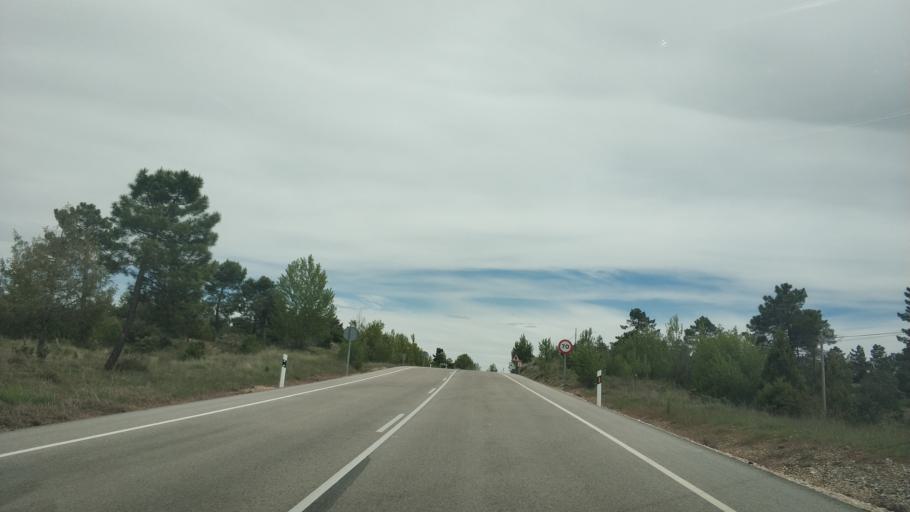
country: ES
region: Castille and Leon
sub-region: Provincia de Soria
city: Valdenebro
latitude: 41.5446
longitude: -2.9580
